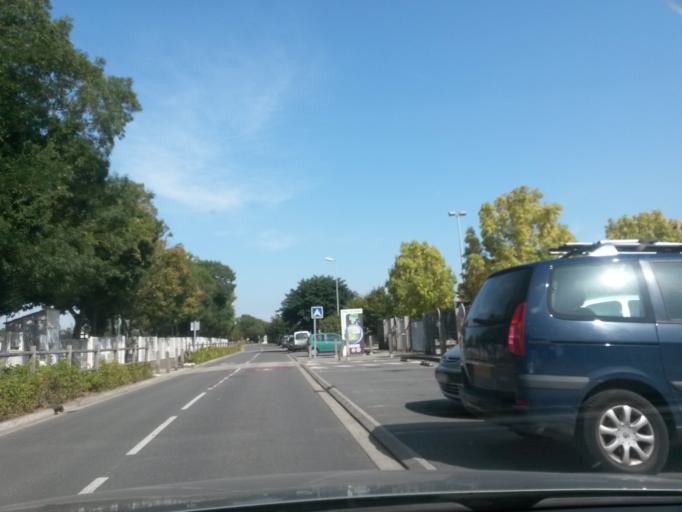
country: FR
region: Poitou-Charentes
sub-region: Departement de la Charente-Maritime
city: Saint-Xandre
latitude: 46.2056
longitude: -1.0974
